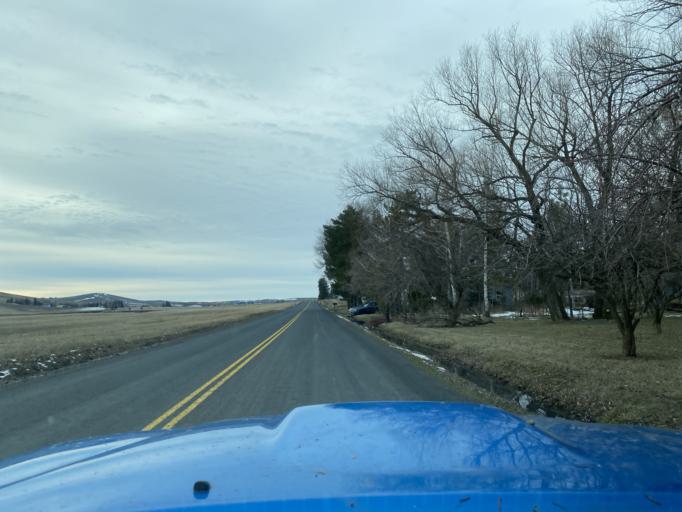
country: US
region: Idaho
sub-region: Latah County
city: Moscow
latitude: 46.7157
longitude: -116.9604
